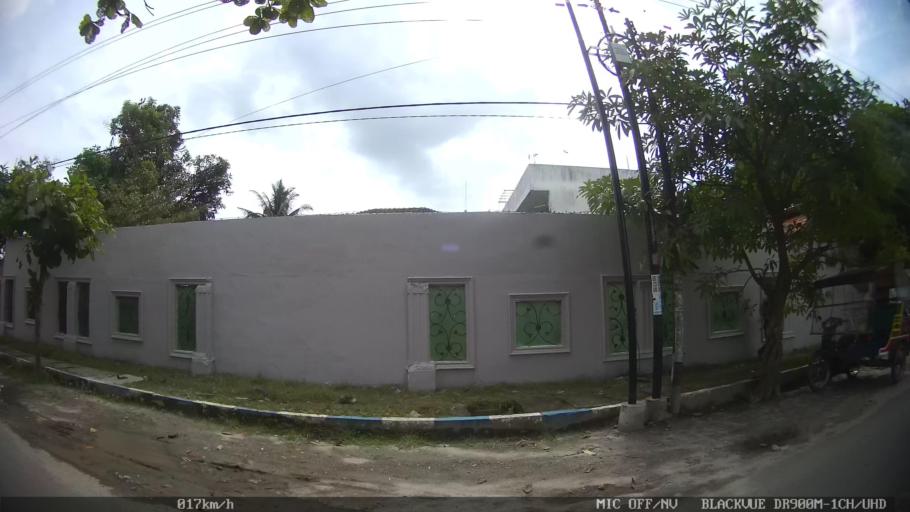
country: ID
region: North Sumatra
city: Percut
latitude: 3.5598
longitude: 98.8671
